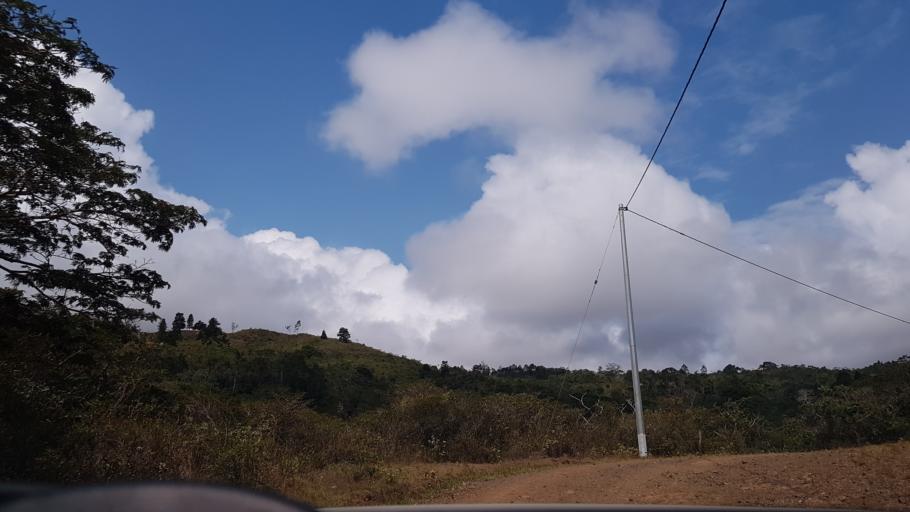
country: CO
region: Valle del Cauca
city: Yumbo
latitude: 3.6537
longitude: -76.5174
